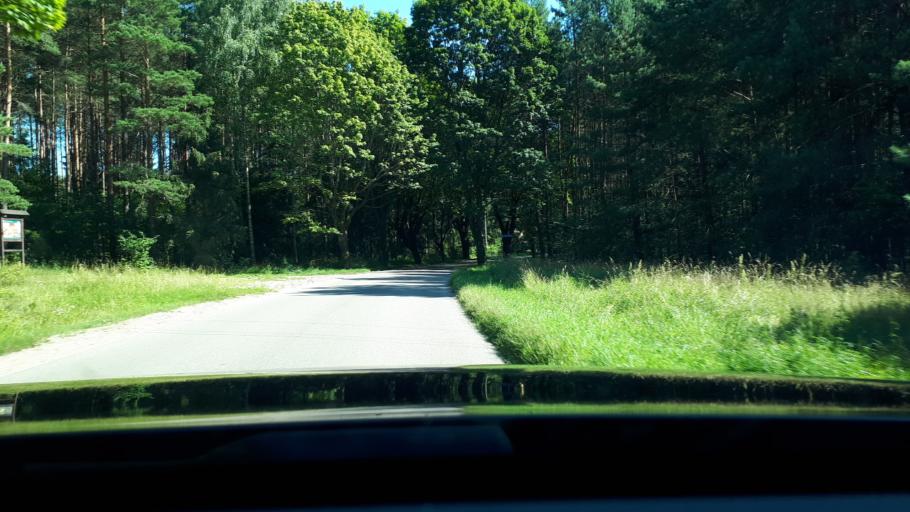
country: PL
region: Warmian-Masurian Voivodeship
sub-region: Powiat olsztynski
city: Stawiguda
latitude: 53.6090
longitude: 20.4225
